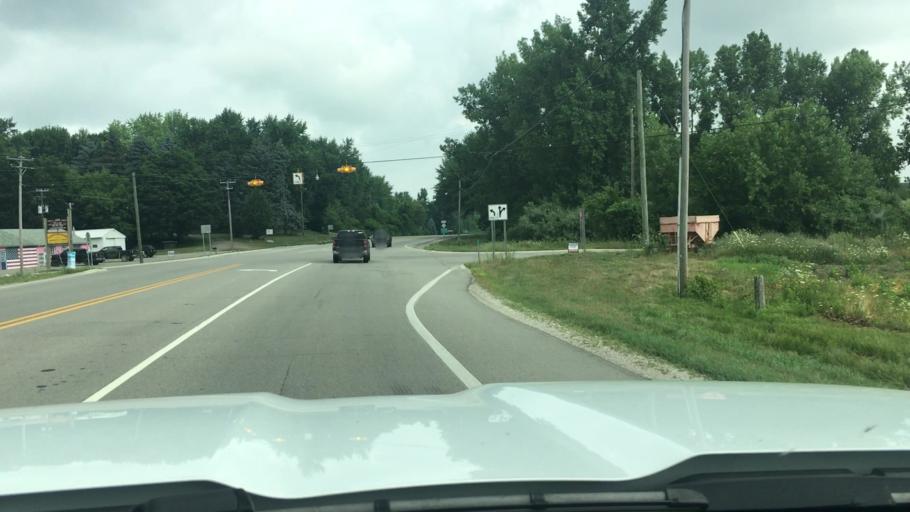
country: US
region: Michigan
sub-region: Lapeer County
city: Imlay City
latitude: 43.0650
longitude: -83.0741
